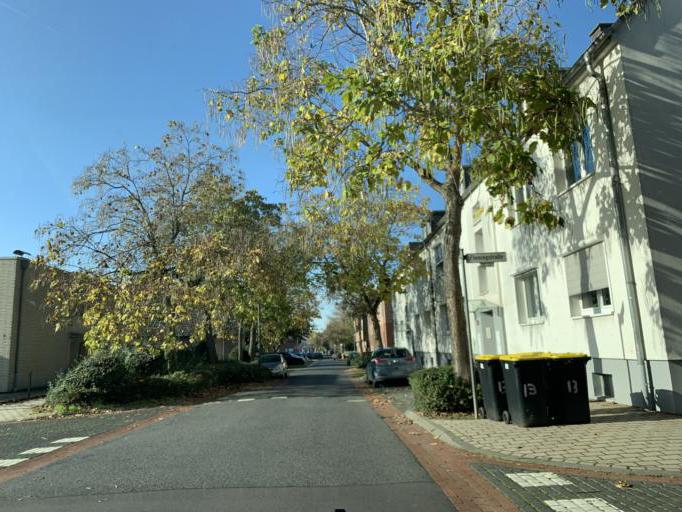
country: DE
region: North Rhine-Westphalia
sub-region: Regierungsbezirk Koln
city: Dueren
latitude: 50.8252
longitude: 6.4667
